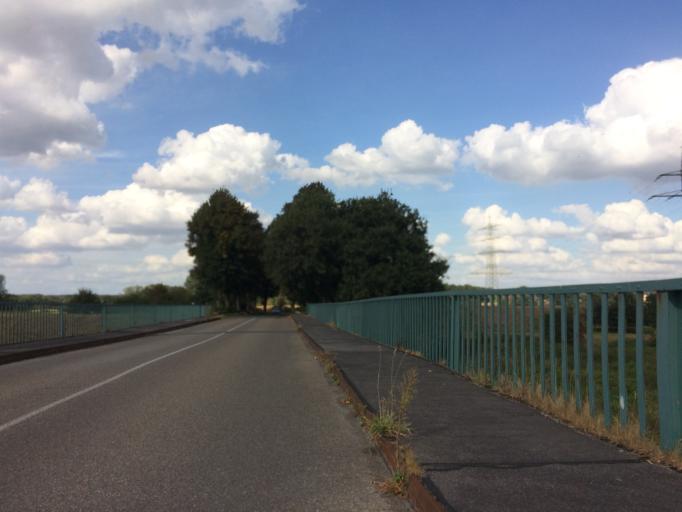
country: DE
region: North Rhine-Westphalia
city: Marl
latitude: 51.6989
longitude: 7.0908
